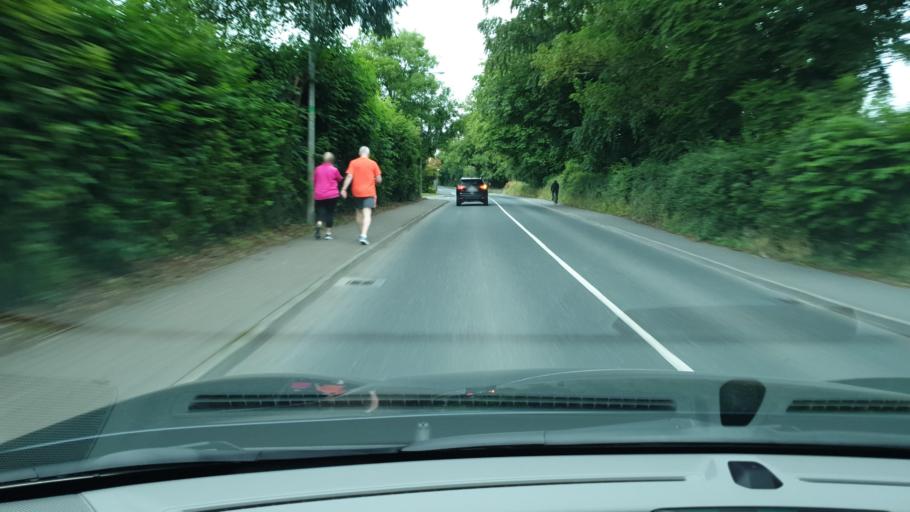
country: IE
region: Leinster
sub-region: An Mhi
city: Dunboyne
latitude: 53.4233
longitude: -6.4834
